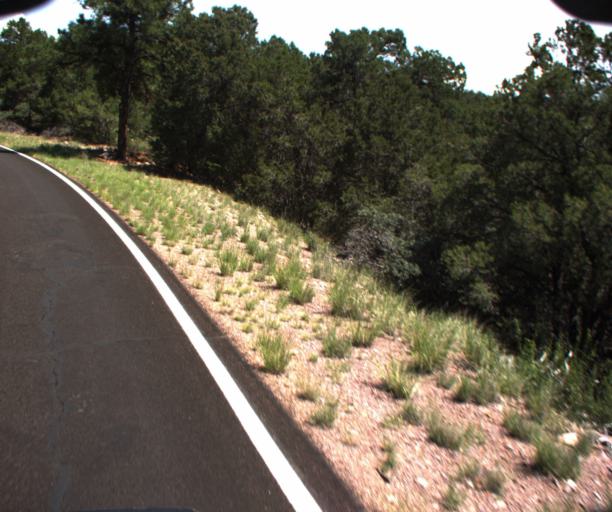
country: US
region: Arizona
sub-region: Greenlee County
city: Morenci
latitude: 33.3816
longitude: -109.3315
